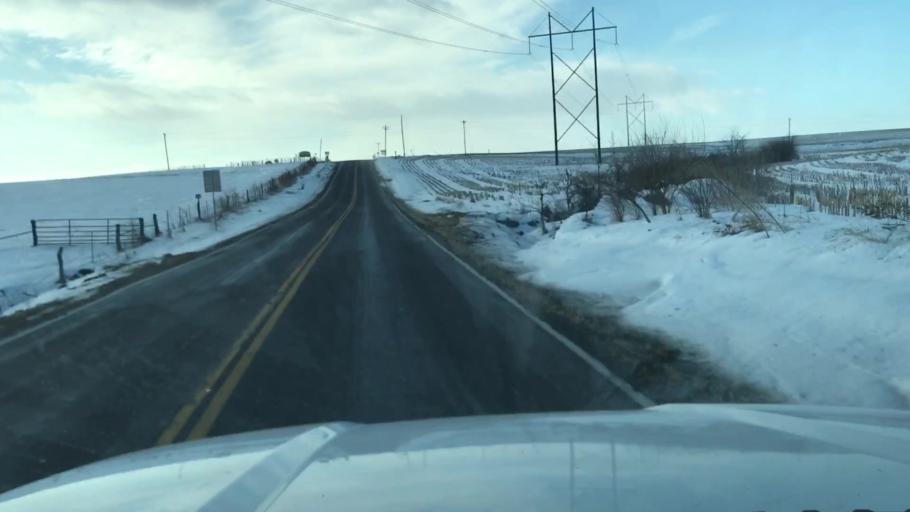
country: US
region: Missouri
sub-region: Nodaway County
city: Maryville
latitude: 40.2019
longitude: -94.9508
